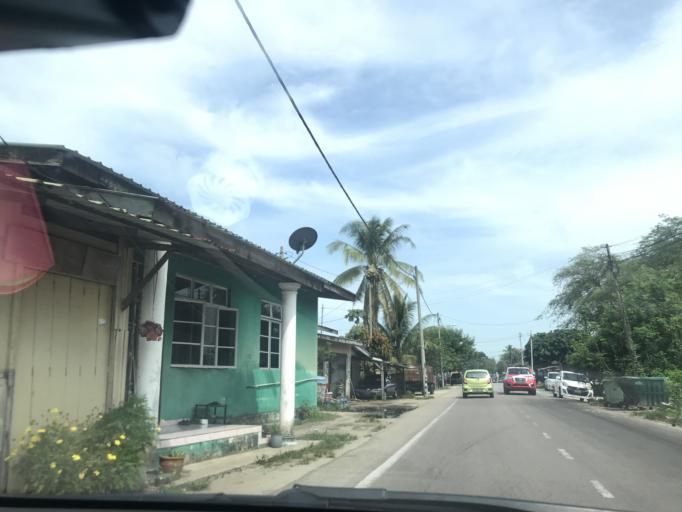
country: MY
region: Kelantan
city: Tumpat
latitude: 6.2010
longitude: 102.1596
